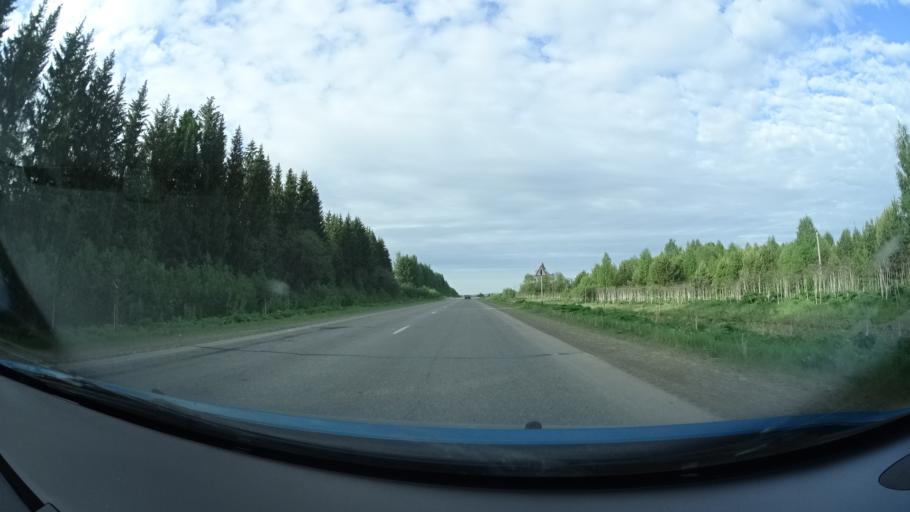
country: RU
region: Perm
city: Osa
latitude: 57.3520
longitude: 55.5965
